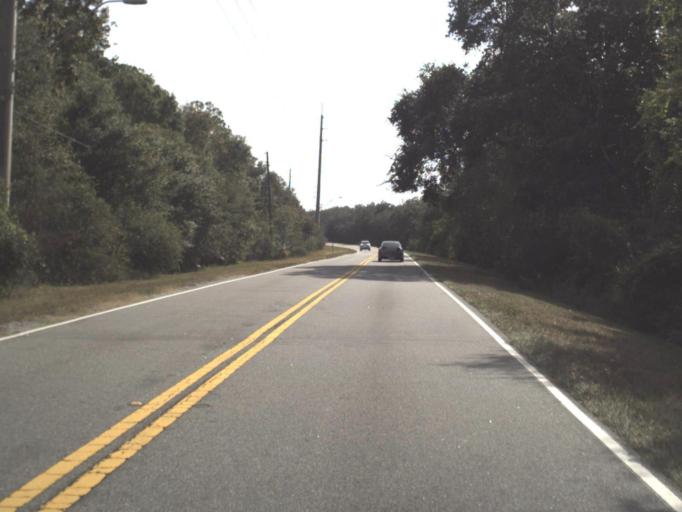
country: US
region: Florida
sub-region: Osceola County
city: Poinciana
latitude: 28.1900
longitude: -81.4657
